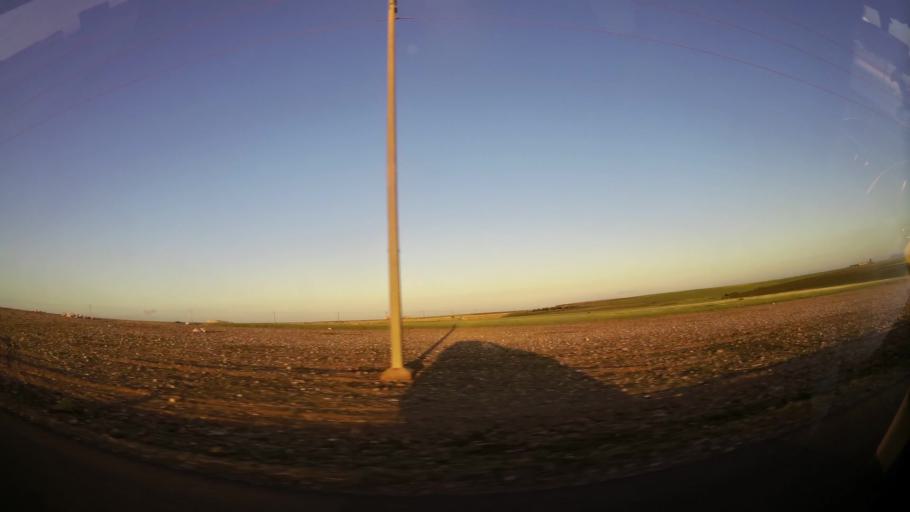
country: MA
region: Marrakech-Tensift-Al Haouz
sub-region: Kelaa-Des-Sraghna
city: Sidi Abdallah
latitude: 32.2369
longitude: -7.9283
